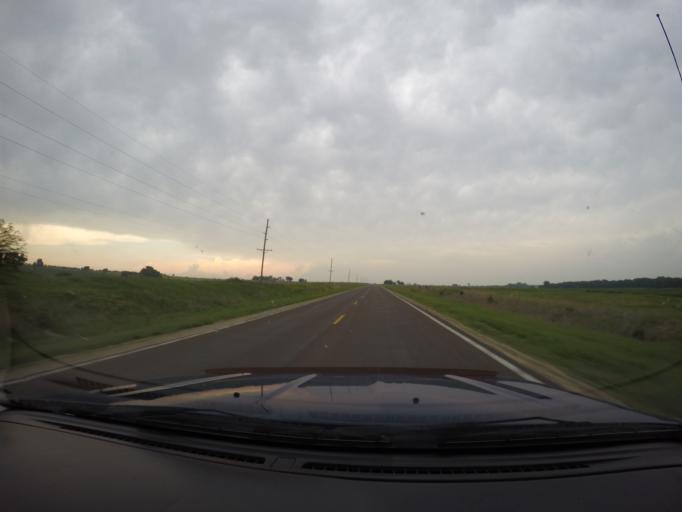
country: US
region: Kansas
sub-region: Clay County
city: Clay Center
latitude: 39.3508
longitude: -96.9233
